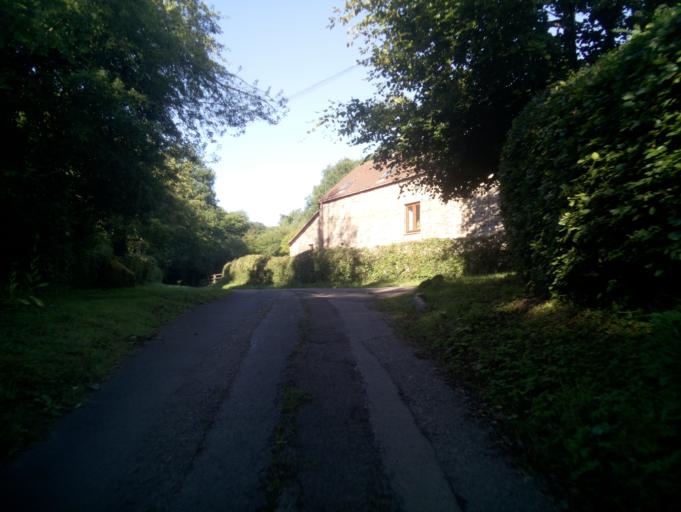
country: GB
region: Wales
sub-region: Monmouthshire
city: Tintern
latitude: 51.6885
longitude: -2.7243
